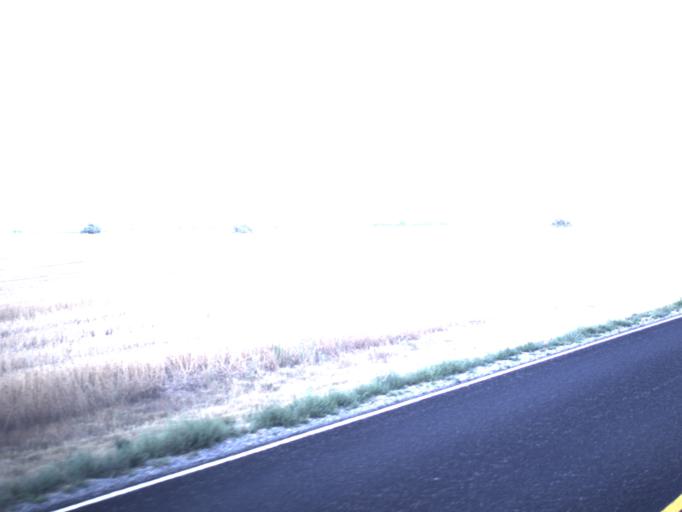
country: US
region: Utah
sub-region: Cache County
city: Lewiston
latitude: 41.9249
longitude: -111.8831
